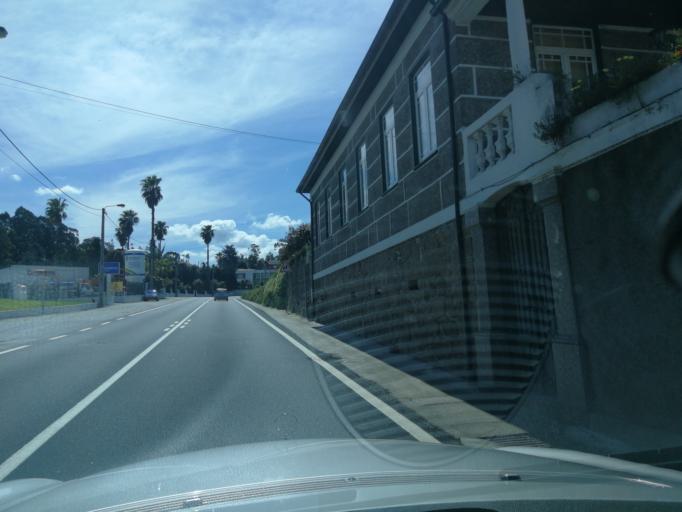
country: PT
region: Braga
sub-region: Vila Nova de Famalicao
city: Calendario
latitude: 41.4248
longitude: -8.5343
